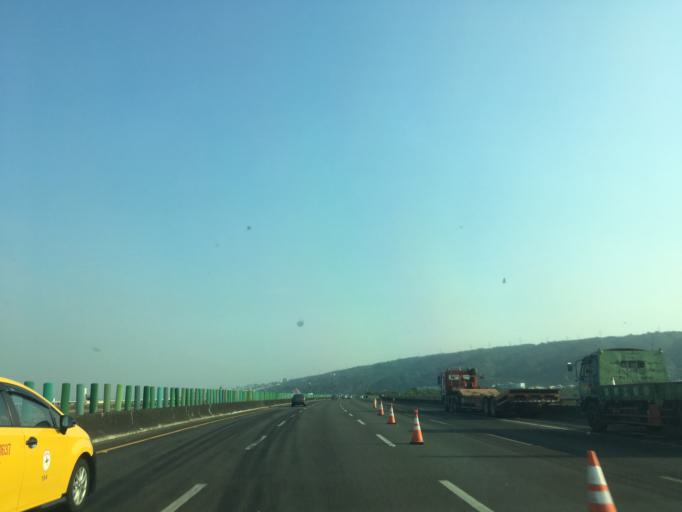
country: TW
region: Taiwan
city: Zhongxing New Village
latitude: 23.9851
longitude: 120.6528
